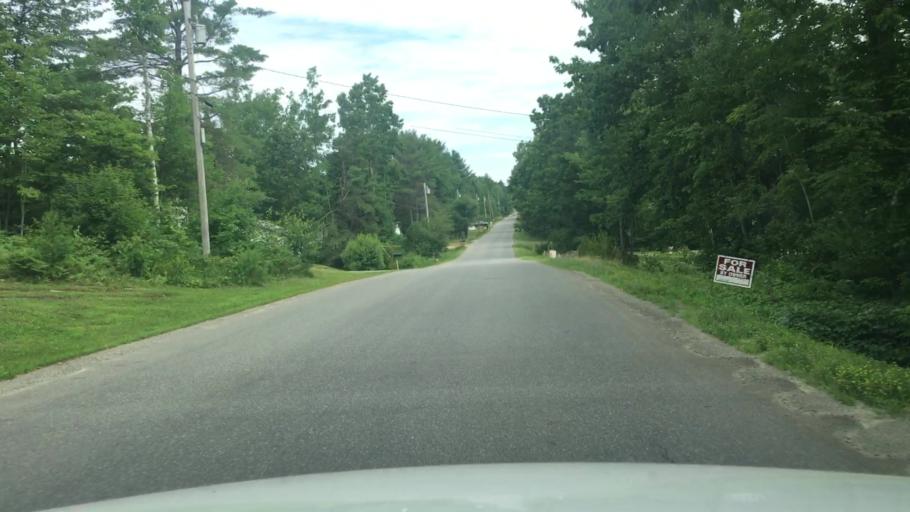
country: US
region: Maine
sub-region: Kennebec County
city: Clinton
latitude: 44.5939
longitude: -69.4713
